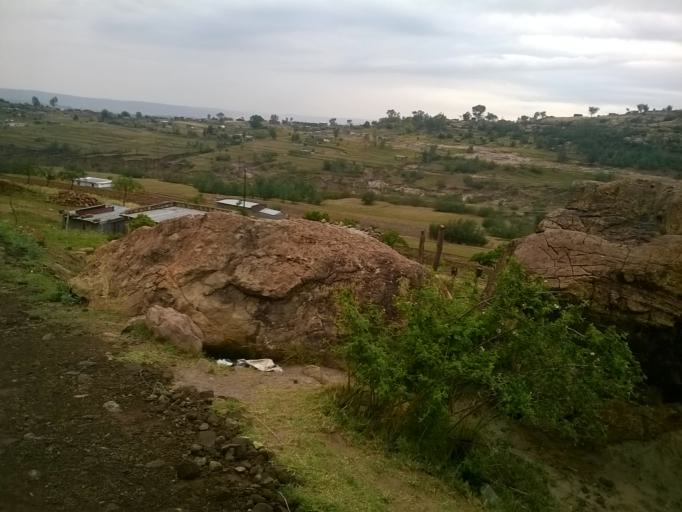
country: LS
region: Berea
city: Teyateyaneng
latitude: -29.1358
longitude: 27.7391
